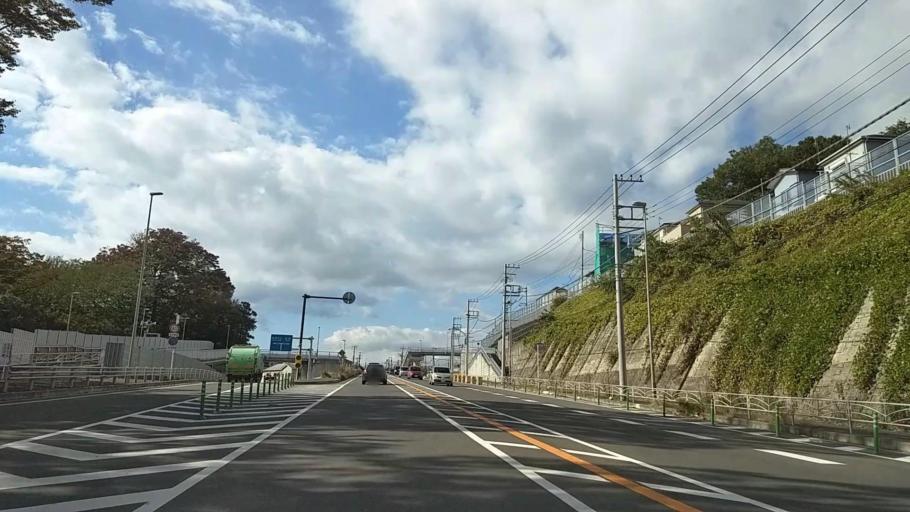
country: JP
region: Kanagawa
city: Hadano
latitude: 35.3803
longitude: 139.2213
